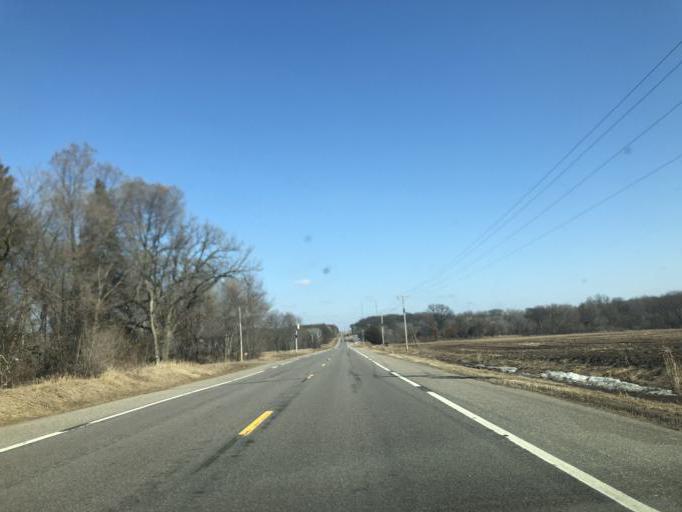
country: US
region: Minnesota
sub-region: Sherburne County
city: Becker
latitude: 45.4298
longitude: -93.8588
